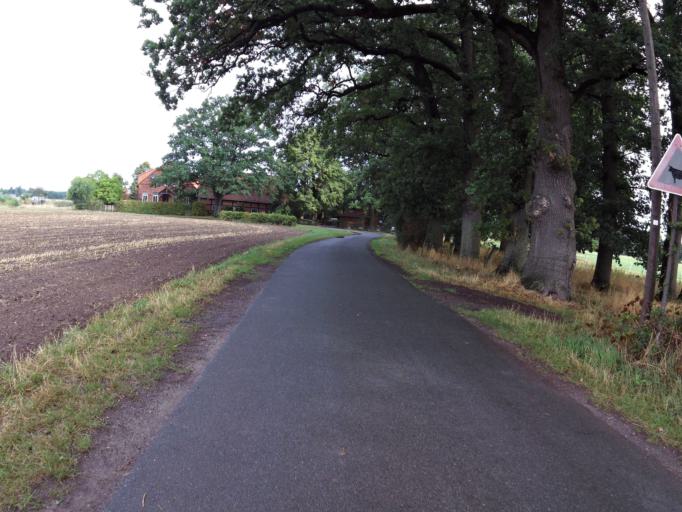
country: DE
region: Lower Saxony
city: Marklohe
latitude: 52.6788
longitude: 9.1715
